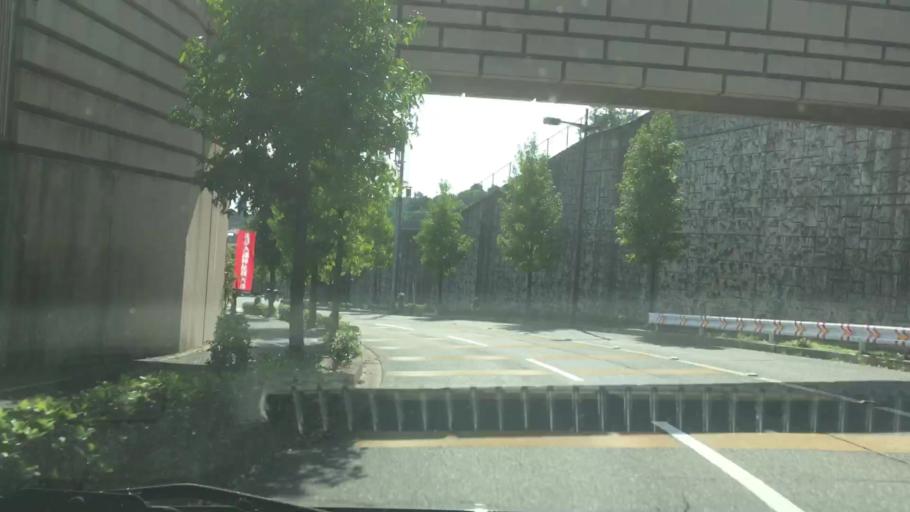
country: JP
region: Hiroshima
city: Hiroshima-shi
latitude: 34.3968
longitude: 132.4134
